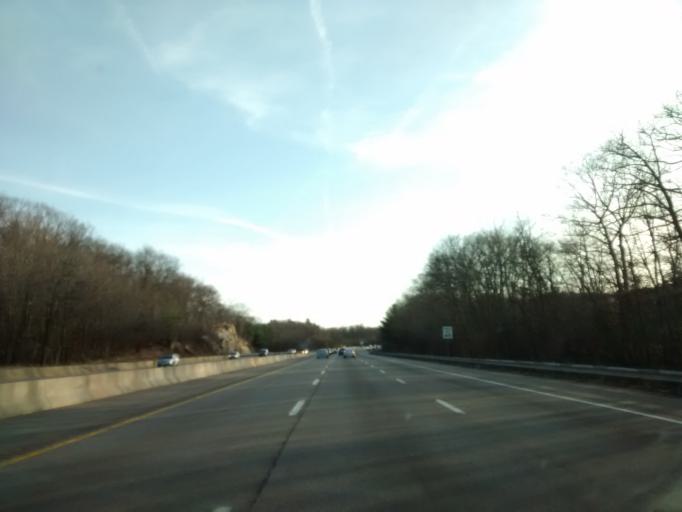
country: US
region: Massachusetts
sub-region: Worcester County
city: Southborough
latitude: 42.2896
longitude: -71.4896
